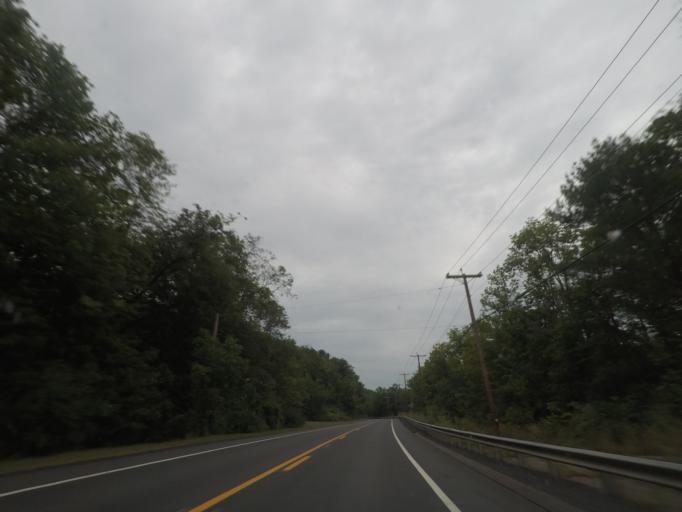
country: US
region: Massachusetts
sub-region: Hampshire County
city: Ware
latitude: 42.2019
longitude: -72.2638
